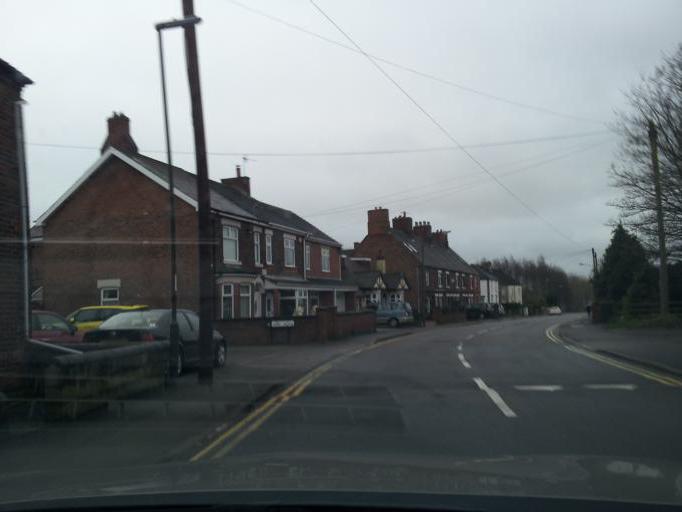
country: GB
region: England
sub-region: Derbyshire
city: Swadlincote
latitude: 52.7662
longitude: -1.5350
